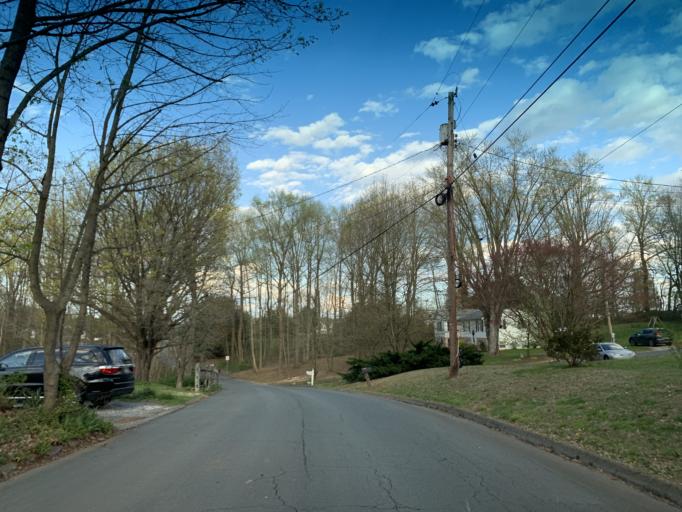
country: US
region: Maryland
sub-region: Harford County
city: South Bel Air
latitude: 39.6107
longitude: -76.2889
